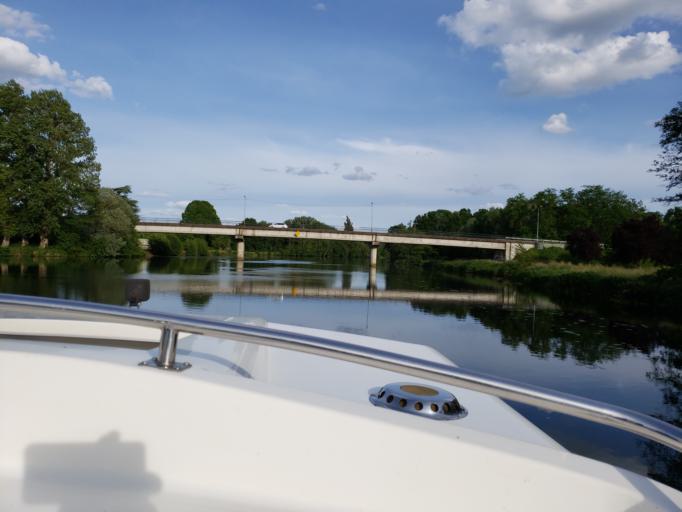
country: FR
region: Bourgogne
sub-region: Departement de l'Yonne
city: Cheny
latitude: 47.9273
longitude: 3.5178
